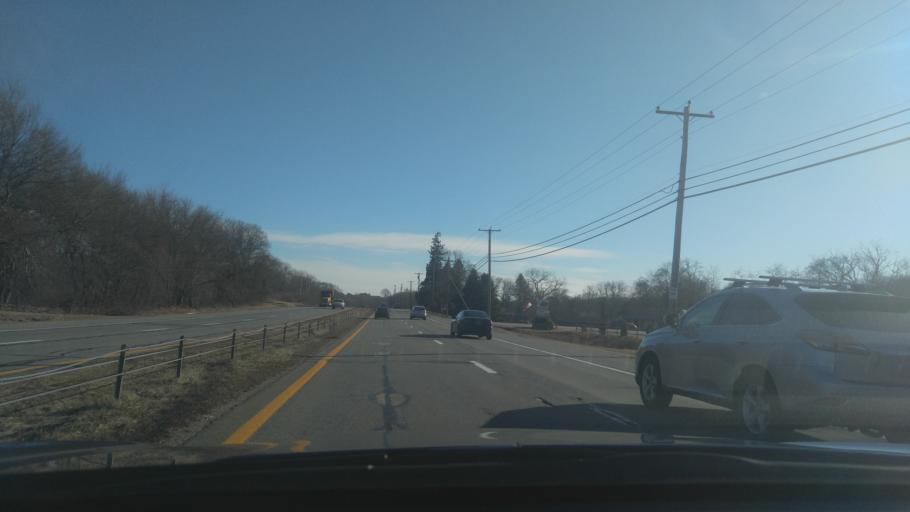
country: US
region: Rhode Island
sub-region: Washington County
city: North Kingstown
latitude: 41.5151
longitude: -71.4612
